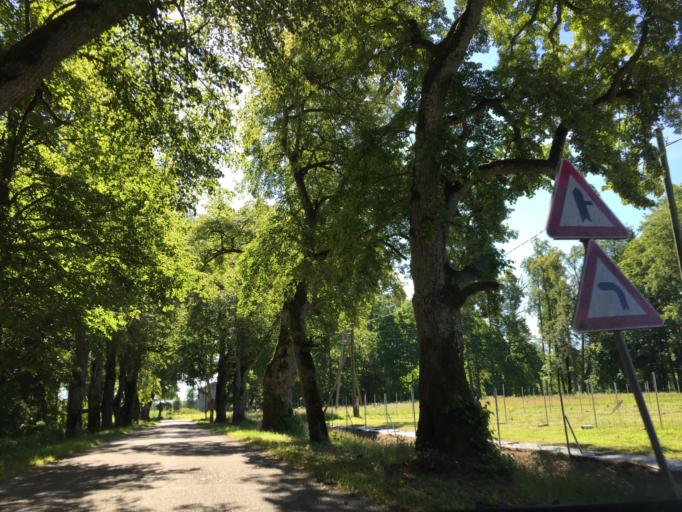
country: LV
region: Kuldigas Rajons
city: Kuldiga
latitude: 57.3231
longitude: 22.0388
